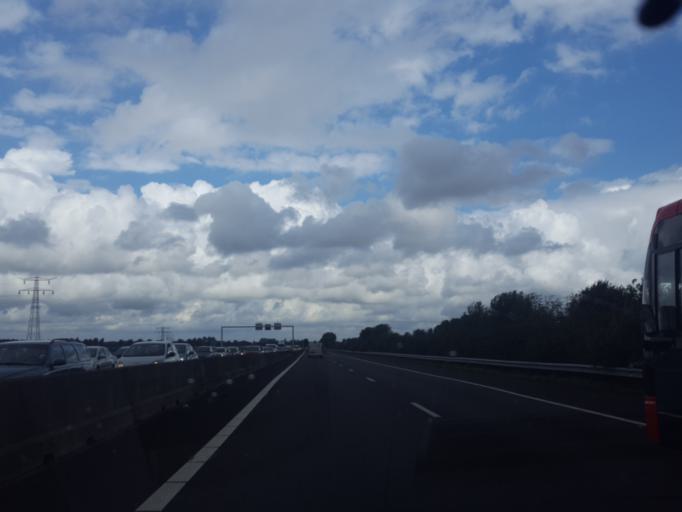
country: NL
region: North Brabant
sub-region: Gemeente Moerdijk
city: Willemstad
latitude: 51.7240
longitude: 4.4060
